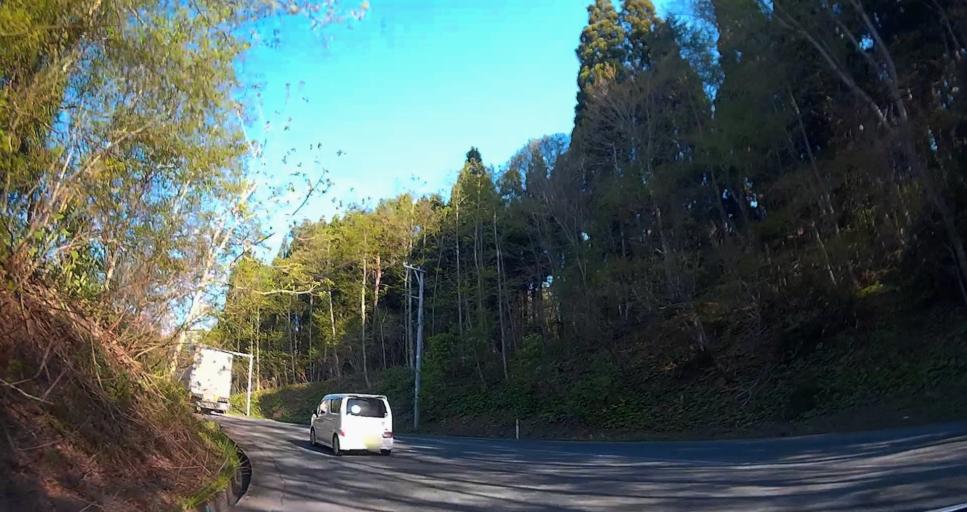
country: JP
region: Aomori
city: Mutsu
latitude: 41.4345
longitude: 141.1327
